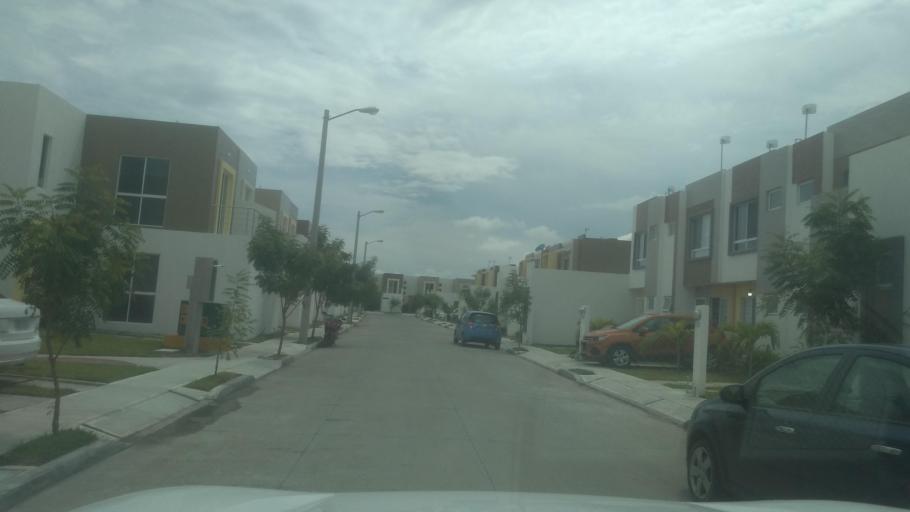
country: MX
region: Veracruz
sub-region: Medellin
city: Fraccionamiento Arboledas San Ramon
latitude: 19.1050
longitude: -96.1645
